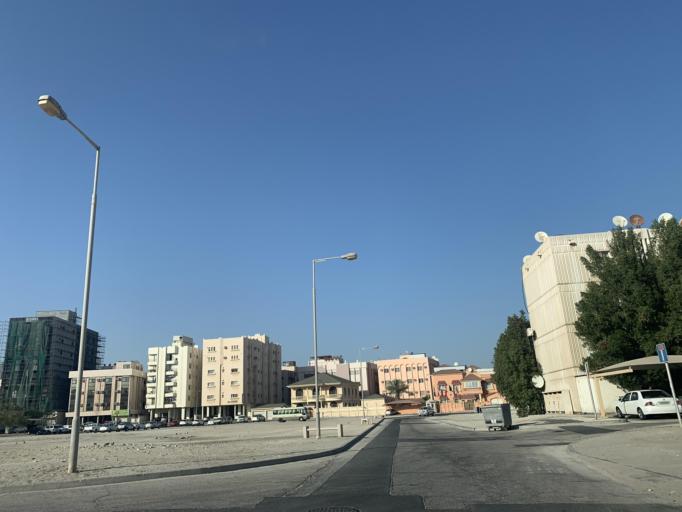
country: BH
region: Manama
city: Manama
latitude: 26.2018
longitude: 50.5864
